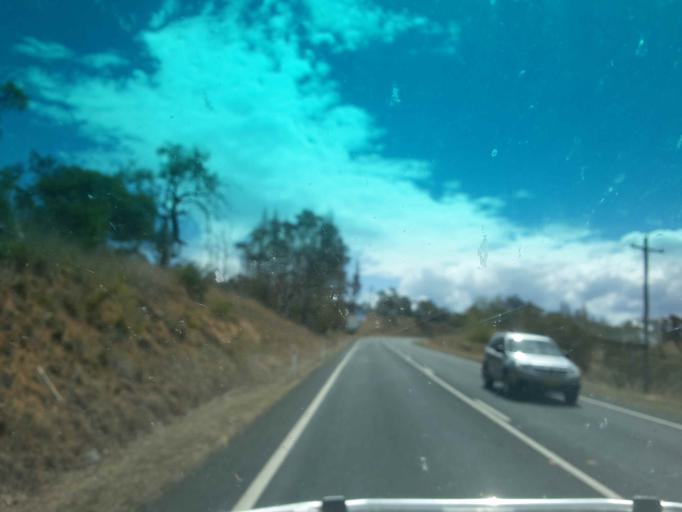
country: AU
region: New South Wales
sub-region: Snowy River
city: Jindabyne
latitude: -36.4268
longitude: 148.6215
